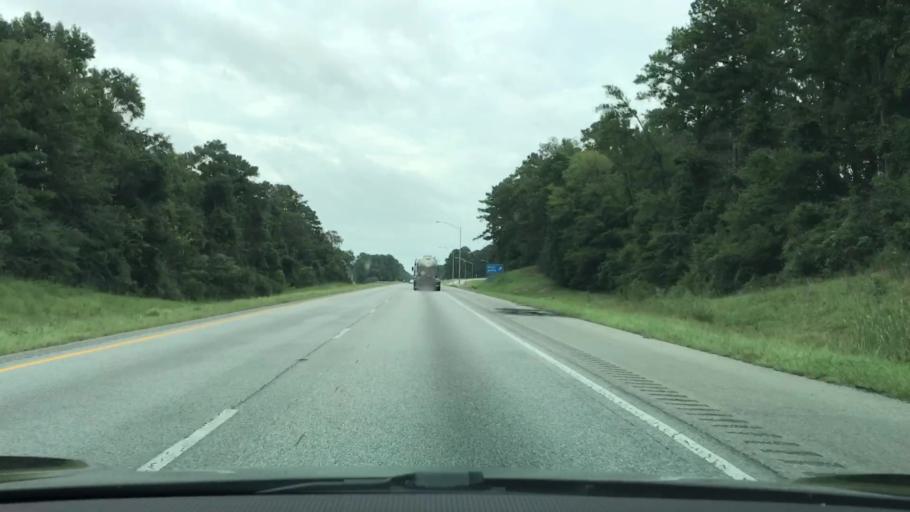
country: US
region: Alabama
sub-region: Macon County
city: Tuskegee
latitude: 32.4955
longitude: -85.6200
